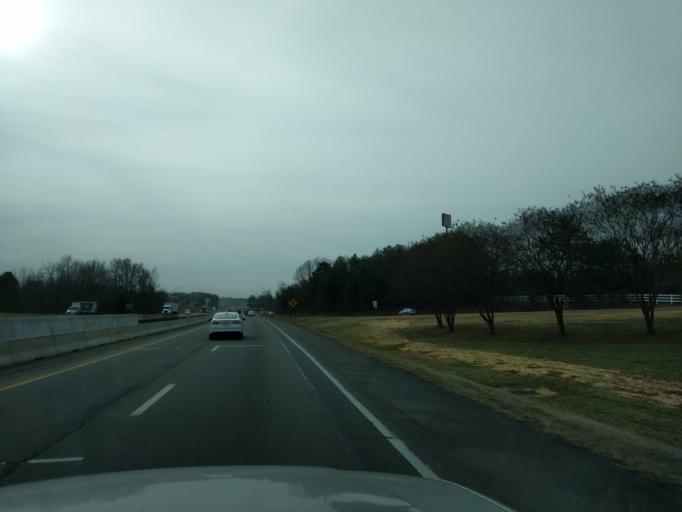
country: US
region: North Carolina
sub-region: Iredell County
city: Mooresville
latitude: 35.5934
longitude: -80.8600
